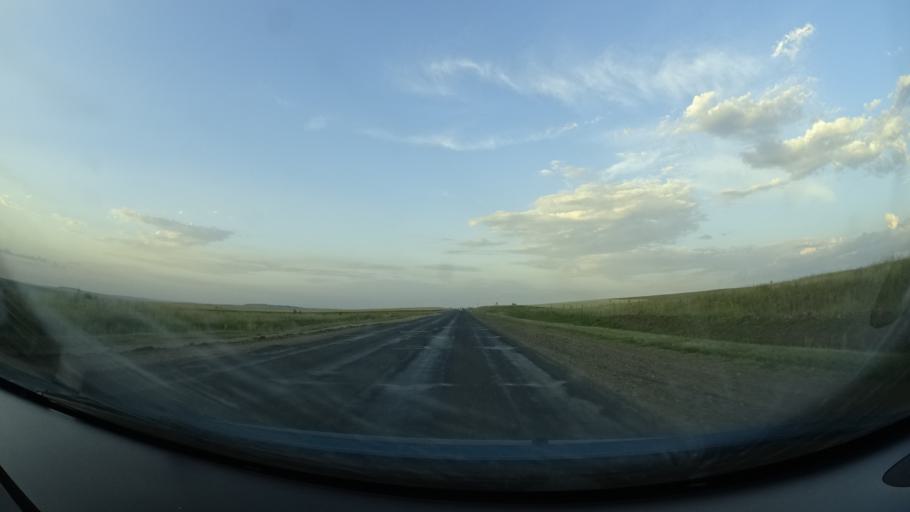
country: RU
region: Orenburg
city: Severnoye
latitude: 54.1072
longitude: 52.5002
